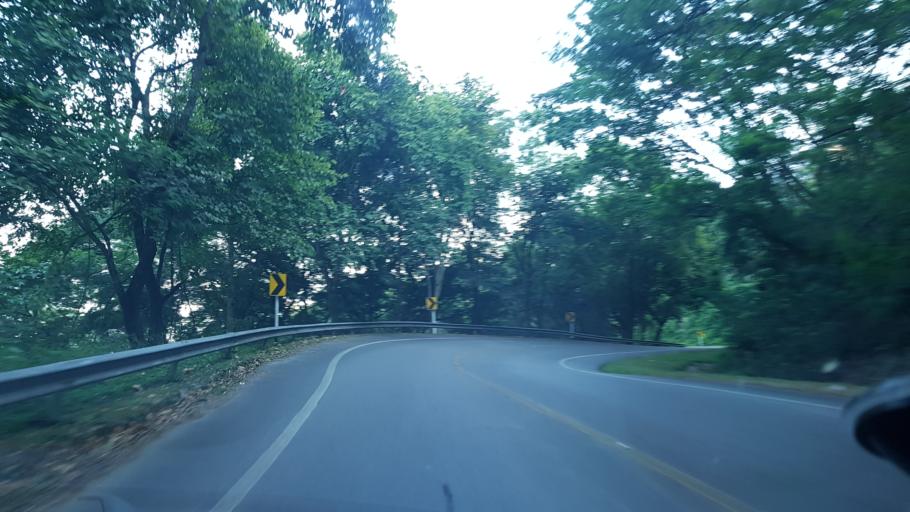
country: TH
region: Chiang Rai
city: Mae Fa Luang
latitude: 20.2955
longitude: 99.8152
